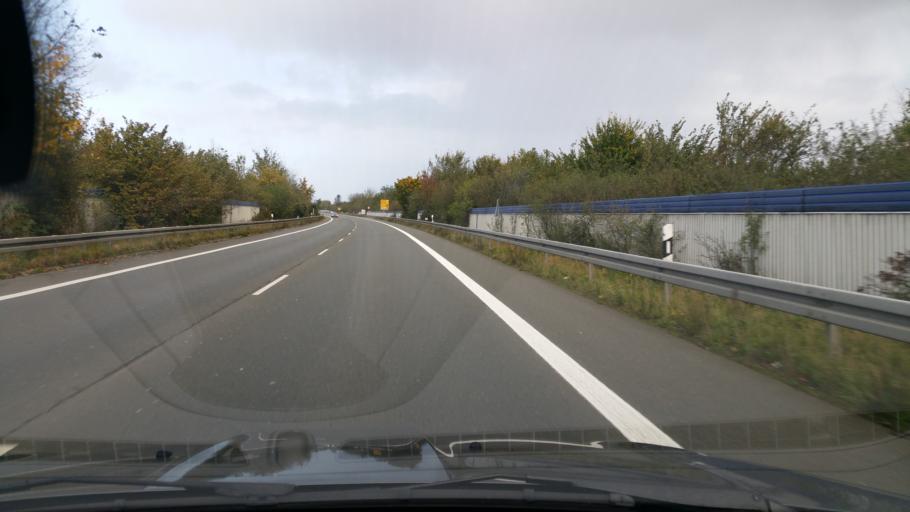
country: DE
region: North Rhine-Westphalia
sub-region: Regierungsbezirk Dusseldorf
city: Bocholt
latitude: 51.8213
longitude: 6.5984
